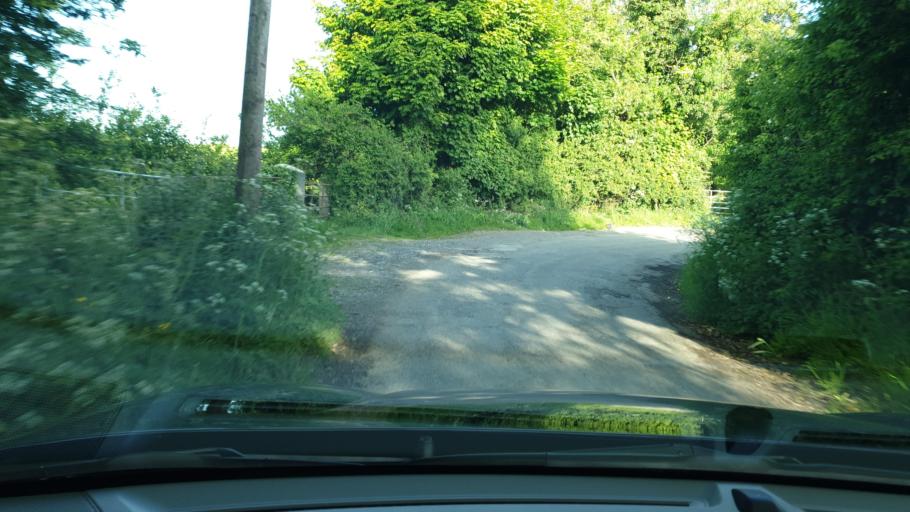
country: IE
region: Leinster
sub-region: An Mhi
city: Ashbourne
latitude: 53.5490
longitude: -6.4144
